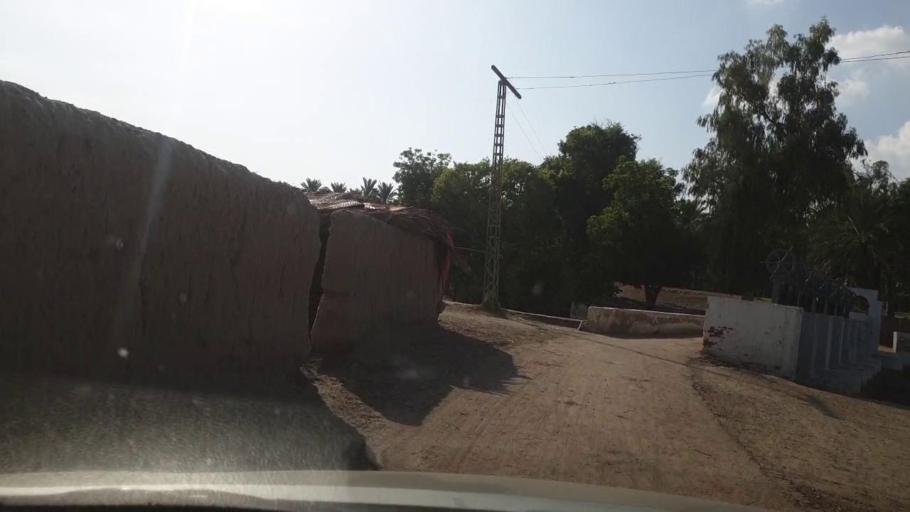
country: PK
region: Sindh
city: Sukkur
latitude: 27.6610
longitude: 68.8336
